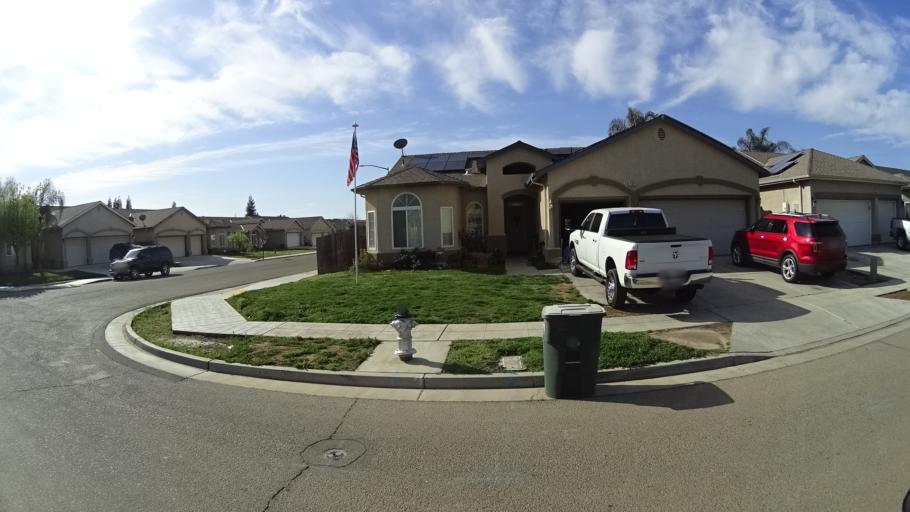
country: US
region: California
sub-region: Fresno County
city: West Park
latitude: 36.8044
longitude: -119.8968
